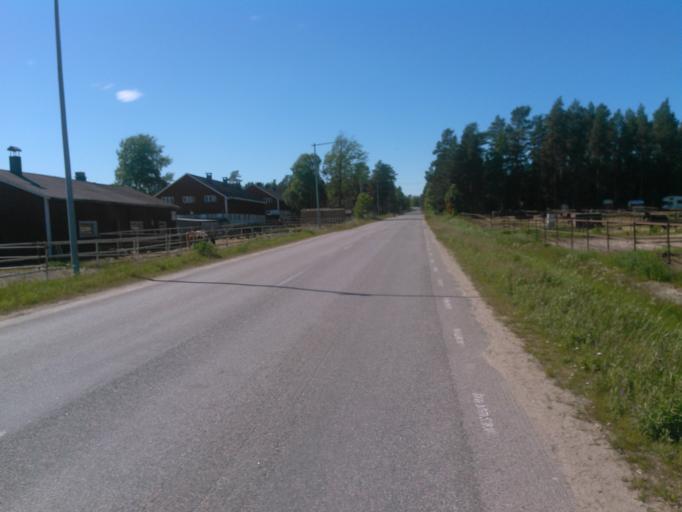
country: SE
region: Vaesterbotten
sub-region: Umea Kommun
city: Roback
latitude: 63.8236
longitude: 20.1815
